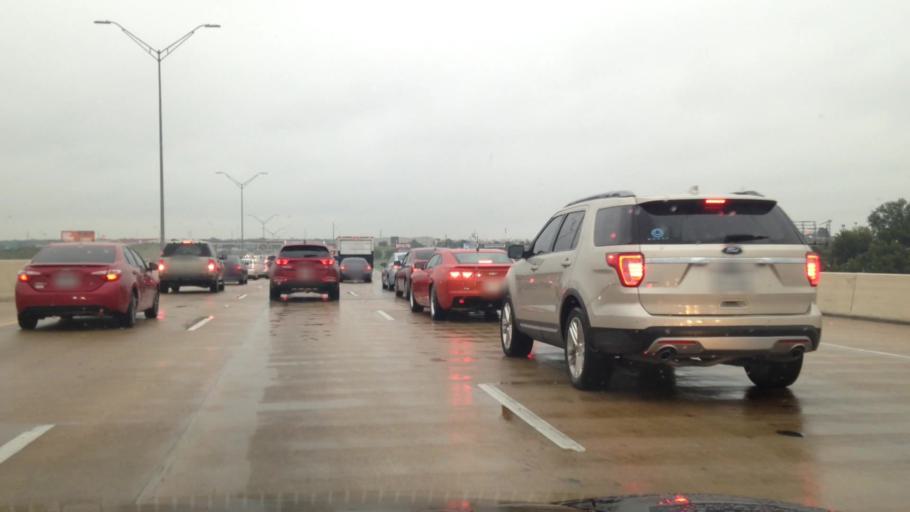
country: US
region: Texas
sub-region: Bexar County
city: Windcrest
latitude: 29.5154
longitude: -98.4107
